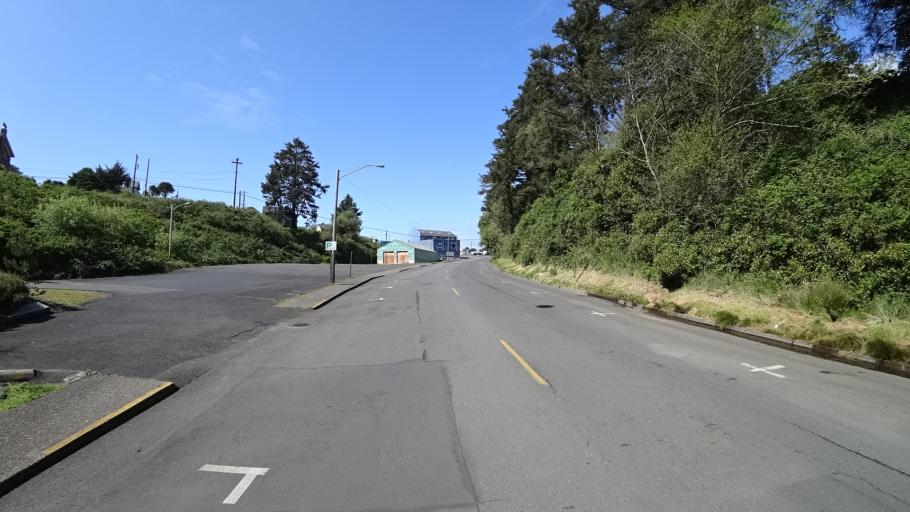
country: US
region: Oregon
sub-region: Lincoln County
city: Newport
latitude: 44.6304
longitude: -124.0555
